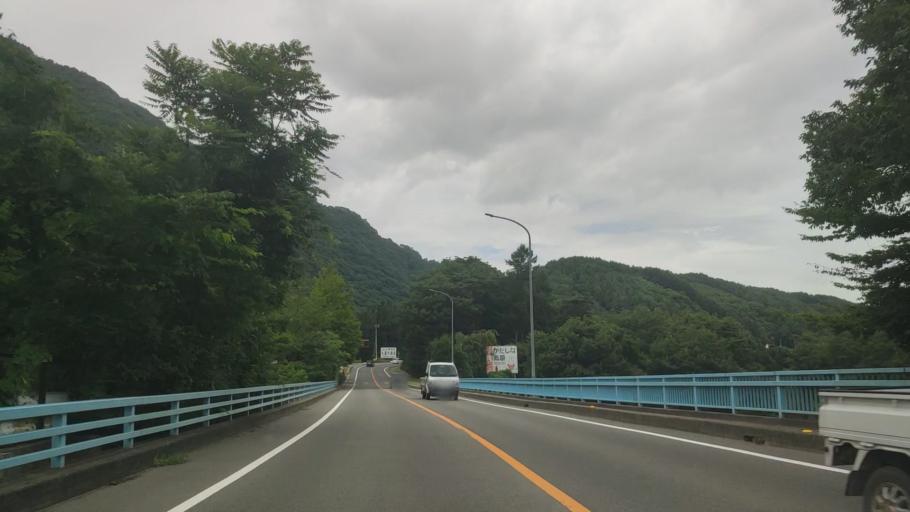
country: JP
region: Gunma
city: Numata
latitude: 36.7110
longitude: 139.2100
